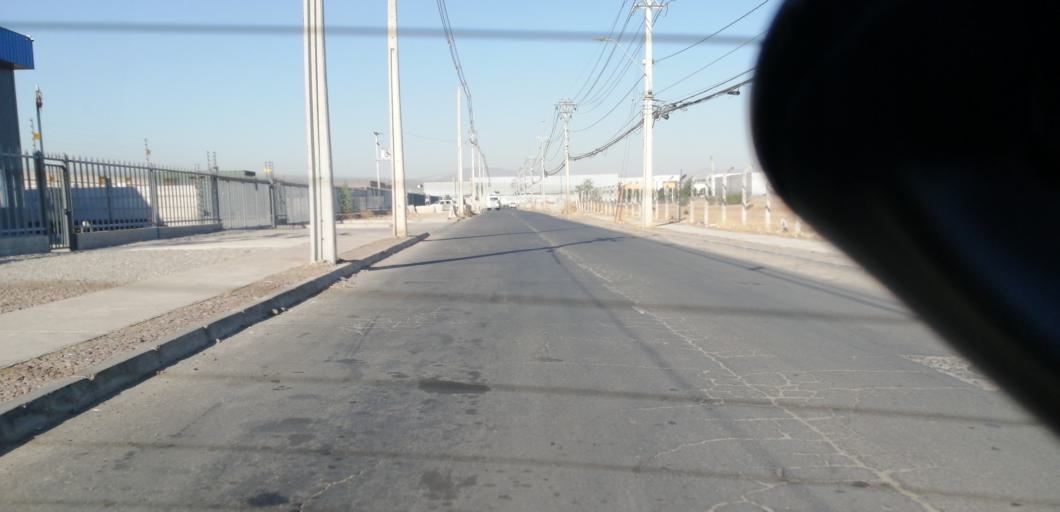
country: CL
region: Santiago Metropolitan
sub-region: Provincia de Santiago
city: Lo Prado
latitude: -33.3797
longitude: -70.7653
